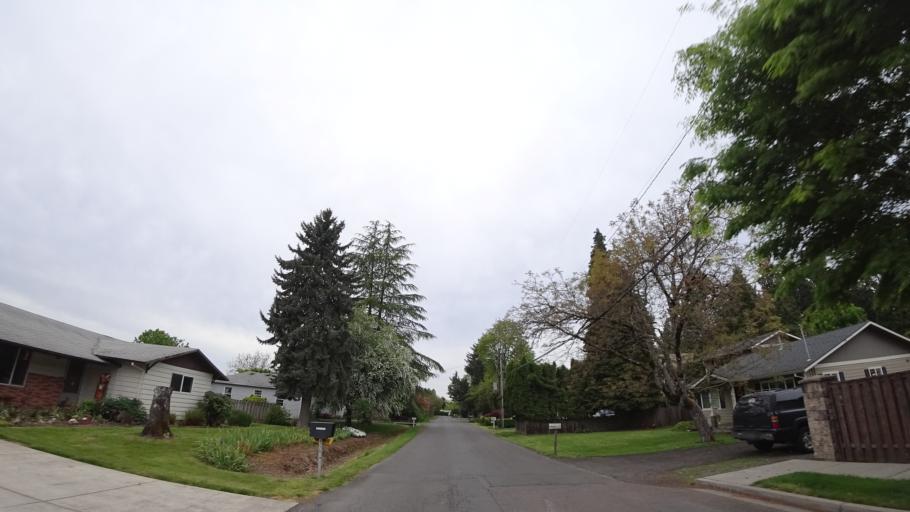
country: US
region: Oregon
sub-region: Washington County
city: Hillsboro
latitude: 45.5031
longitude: -122.9339
